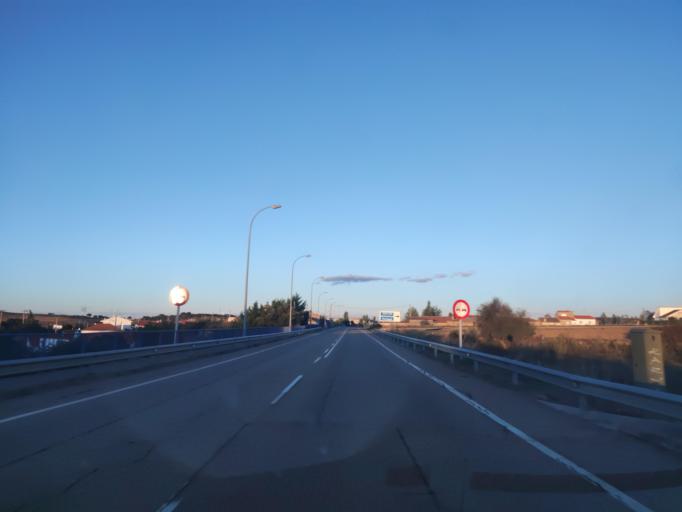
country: ES
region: Castille and Leon
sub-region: Provincia de Salamanca
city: Martin de Yeltes
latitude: 40.7744
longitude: -6.2904
